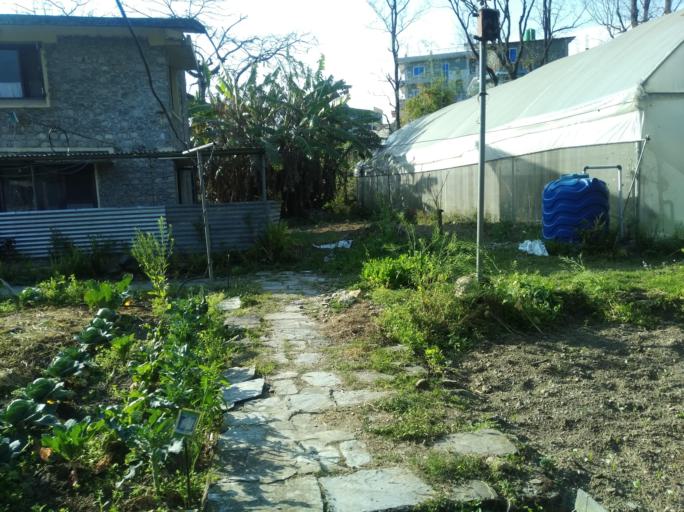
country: NP
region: Western Region
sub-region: Gandaki Zone
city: Pokhara
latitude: 28.2544
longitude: 83.9741
